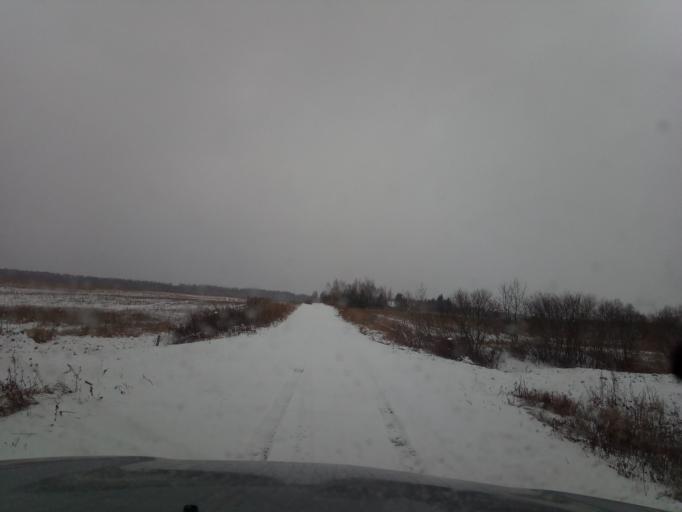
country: LT
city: Ramygala
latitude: 55.5882
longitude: 24.3619
